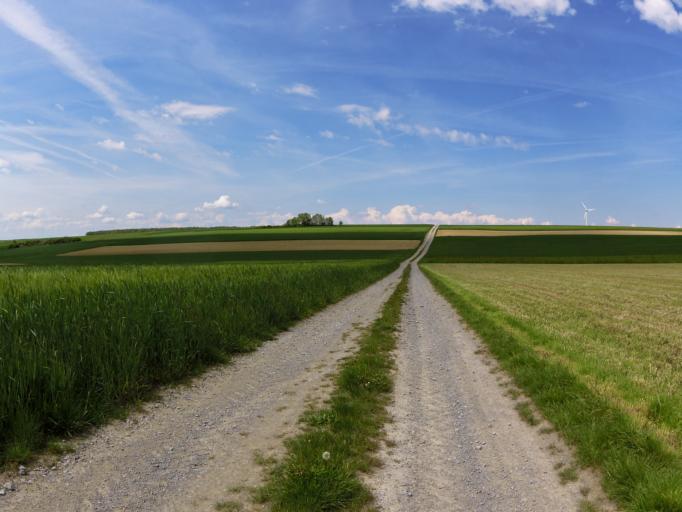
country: DE
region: Bavaria
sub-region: Regierungsbezirk Unterfranken
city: Theilheim
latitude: 49.7338
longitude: 10.0449
